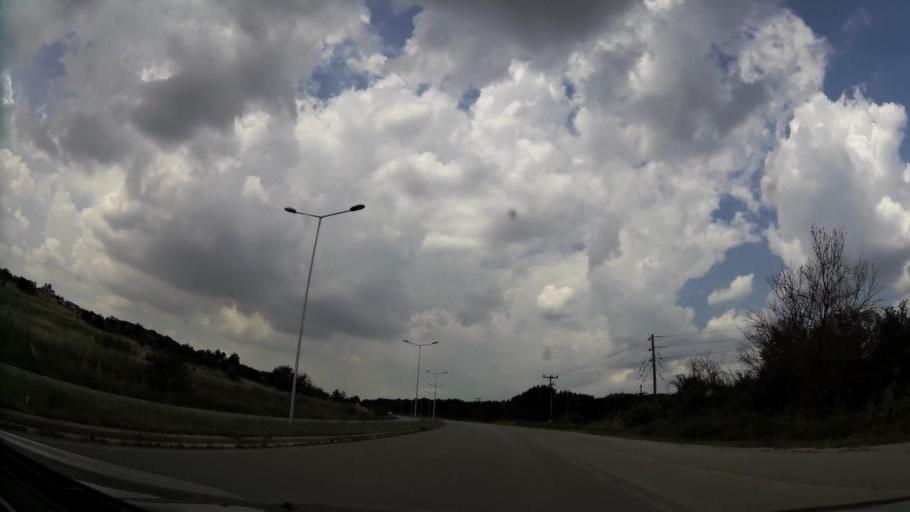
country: GR
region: West Macedonia
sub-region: Nomos Kozanis
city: Koila
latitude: 40.3175
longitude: 21.8274
